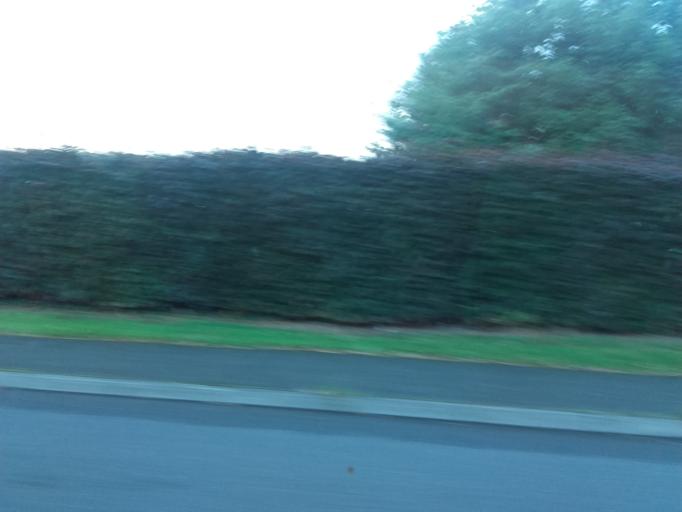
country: IE
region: Leinster
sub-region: Kildare
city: Droichead Nua
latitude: 53.1794
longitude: -6.7798
